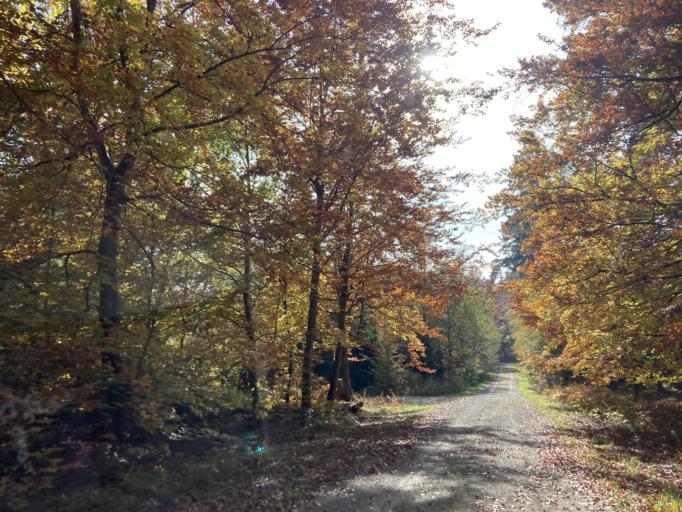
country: DE
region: Baden-Wuerttemberg
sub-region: Tuebingen Region
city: Bodelshausen
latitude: 48.4210
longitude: 8.9468
